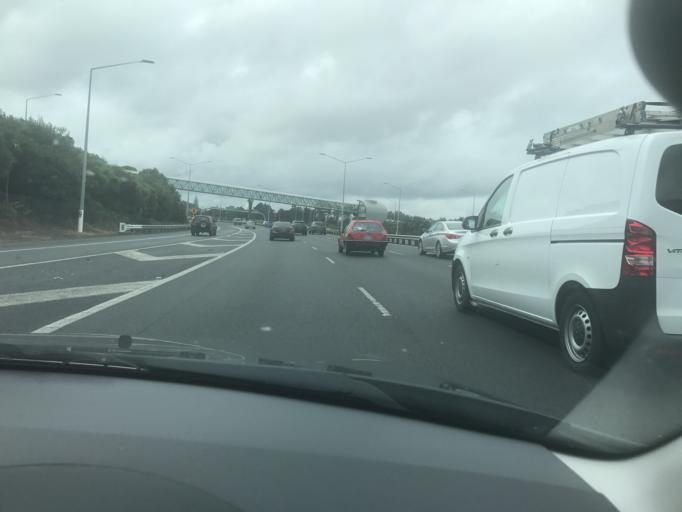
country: NZ
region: Auckland
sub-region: Auckland
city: North Shore
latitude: -36.7992
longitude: 174.7611
